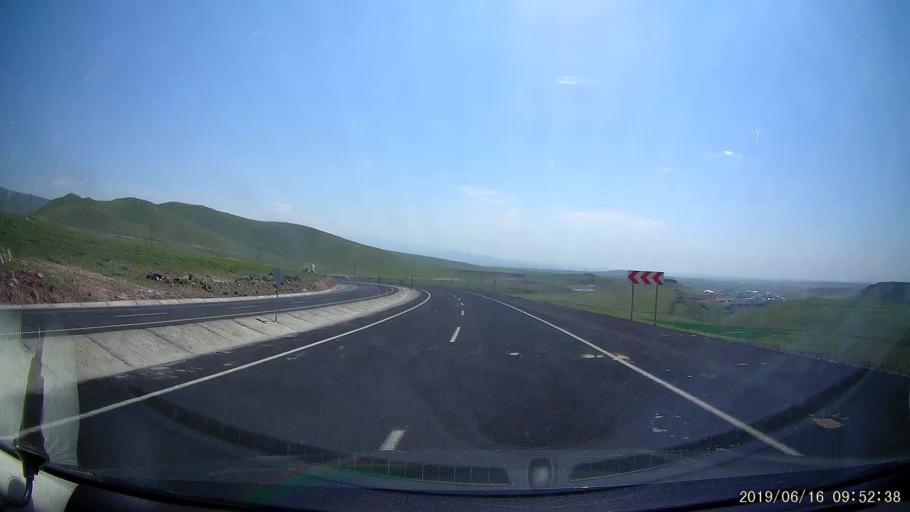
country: TR
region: Kars
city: Digor
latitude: 40.3936
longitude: 43.3914
